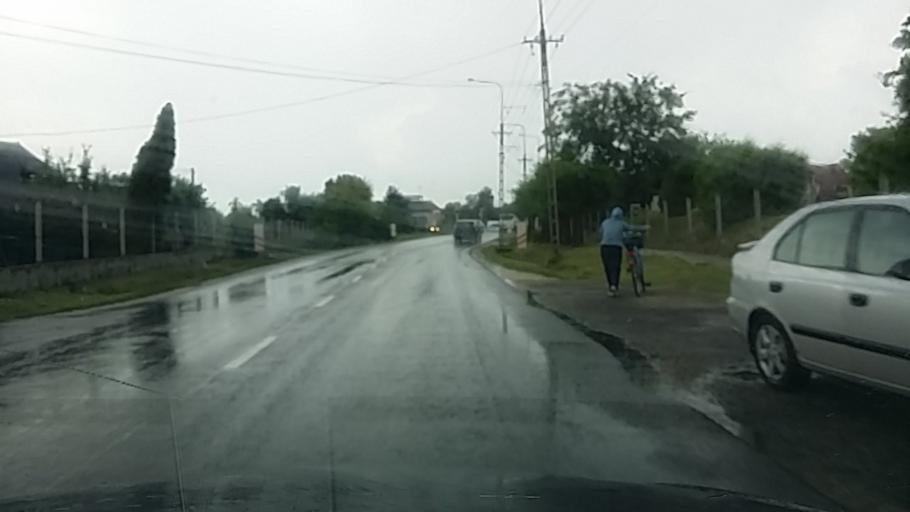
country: HU
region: Pest
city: Ocsa
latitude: 47.2965
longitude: 19.2379
